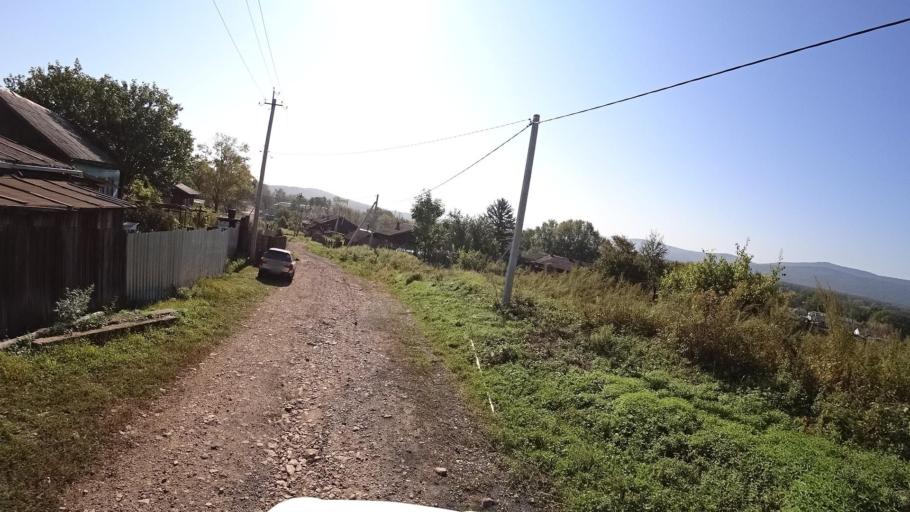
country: RU
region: Jewish Autonomous Oblast
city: Bira
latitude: 49.0028
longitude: 132.4606
